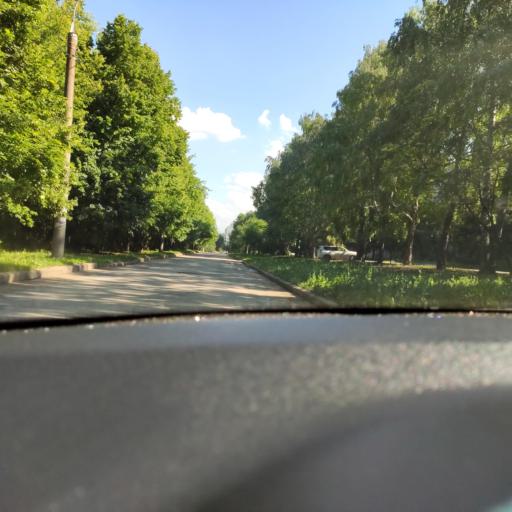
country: RU
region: Samara
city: Petra-Dubrava
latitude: 53.3055
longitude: 50.2743
